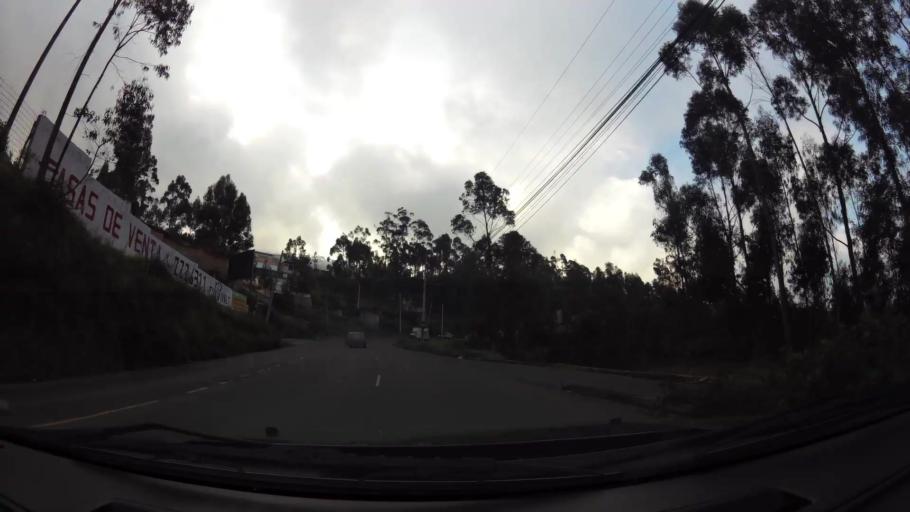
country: EC
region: Pichincha
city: Quito
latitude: -0.2666
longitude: -78.4943
